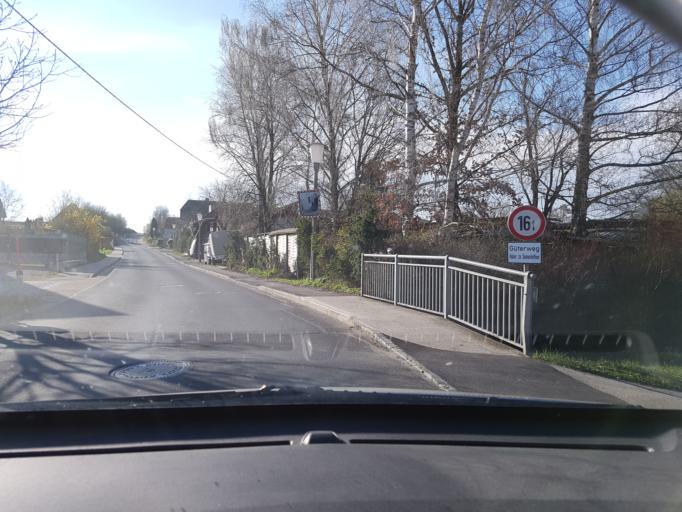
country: AT
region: Upper Austria
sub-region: Politischer Bezirk Linz-Land
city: Asten
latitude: 48.2069
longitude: 14.4205
